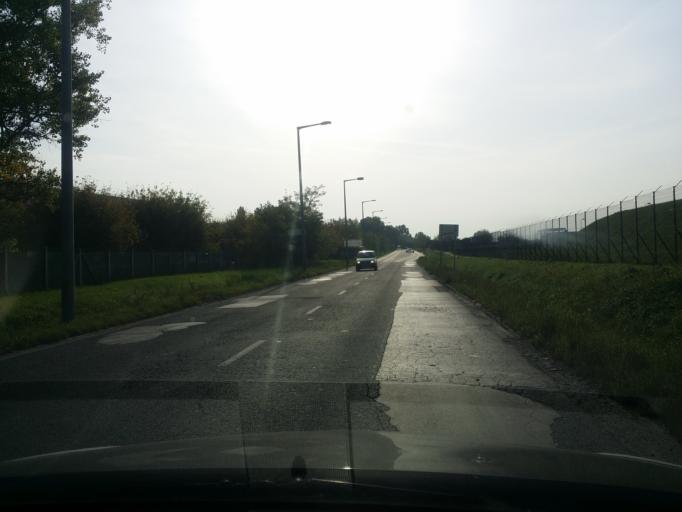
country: HU
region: Budapest
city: Budapest XV. keruelet
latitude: 47.5824
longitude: 19.1366
